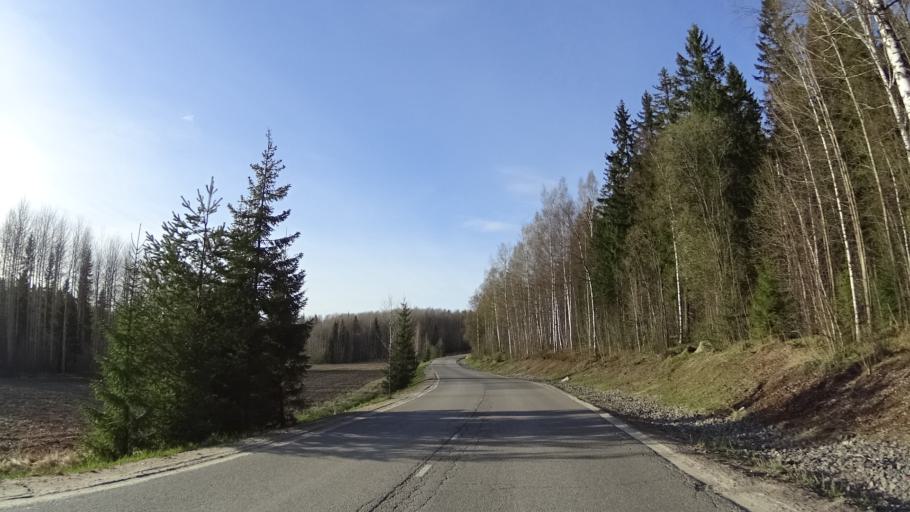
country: FI
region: Uusimaa
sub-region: Helsinki
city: Kilo
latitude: 60.2967
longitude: 24.7966
